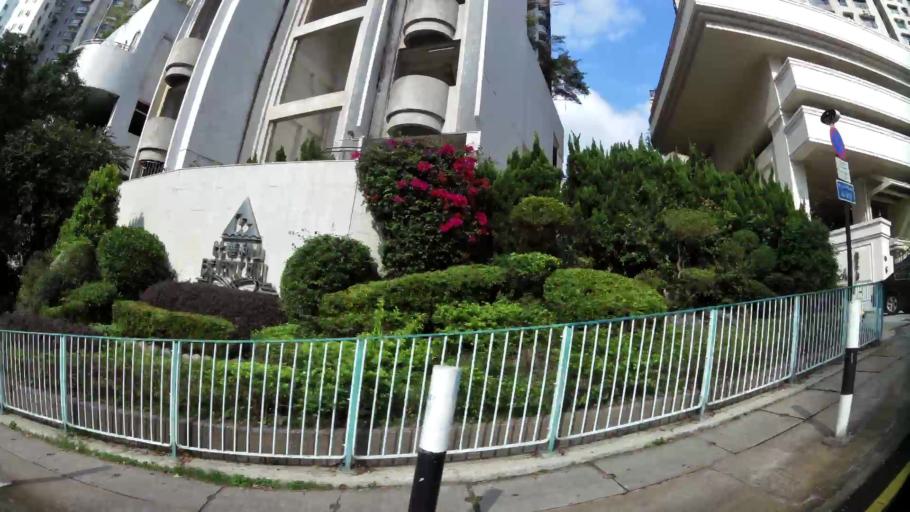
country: HK
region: Wanchai
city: Wan Chai
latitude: 22.2731
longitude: 114.1859
